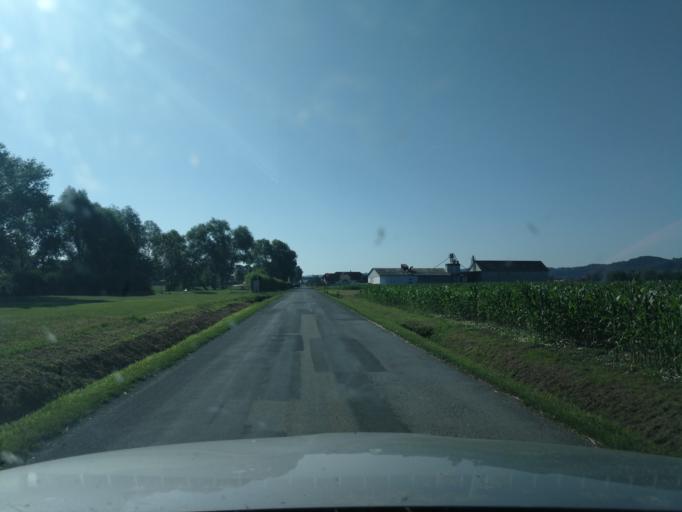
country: AT
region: Burgenland
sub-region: Politischer Bezirk Jennersdorf
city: Konigsdorf
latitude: 47.0085
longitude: 16.1600
